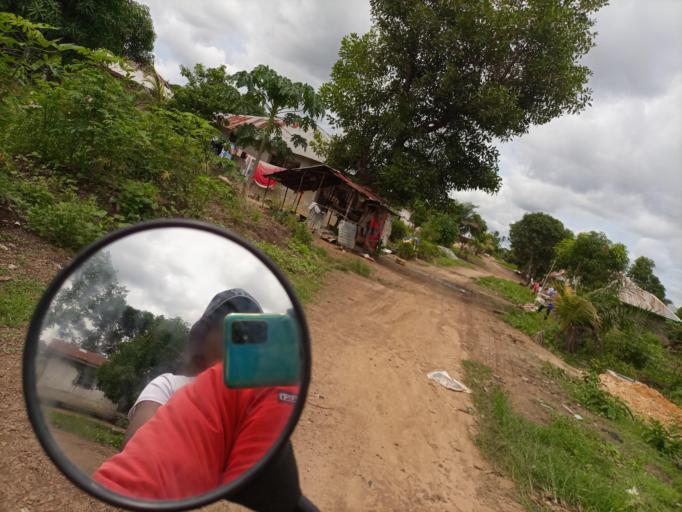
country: SL
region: Southern Province
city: Baoma
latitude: 7.9688
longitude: -11.7120
